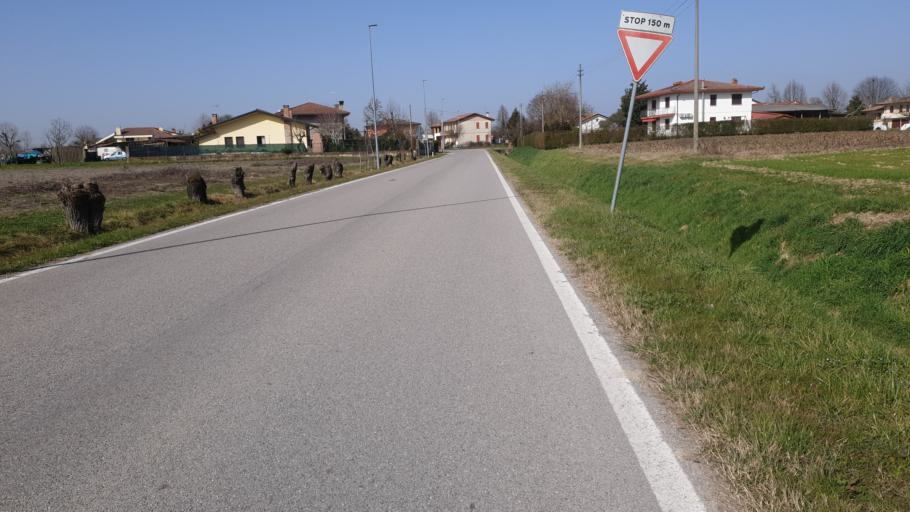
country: IT
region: Veneto
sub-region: Provincia di Padova
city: Cavino
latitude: 45.5016
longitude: 11.8900
